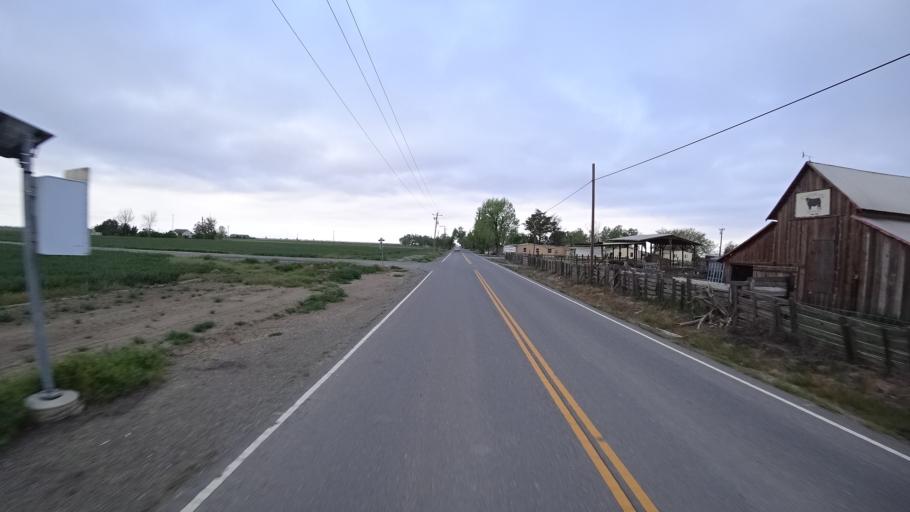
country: US
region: California
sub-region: Colusa County
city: Colusa
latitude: 39.4063
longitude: -122.0150
